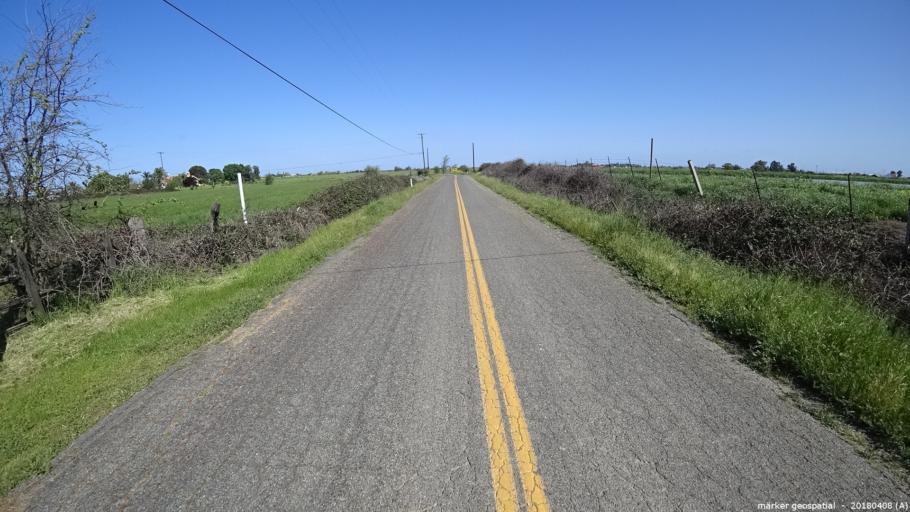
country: US
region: California
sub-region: Sacramento County
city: Laguna
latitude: 38.3385
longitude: -121.4267
